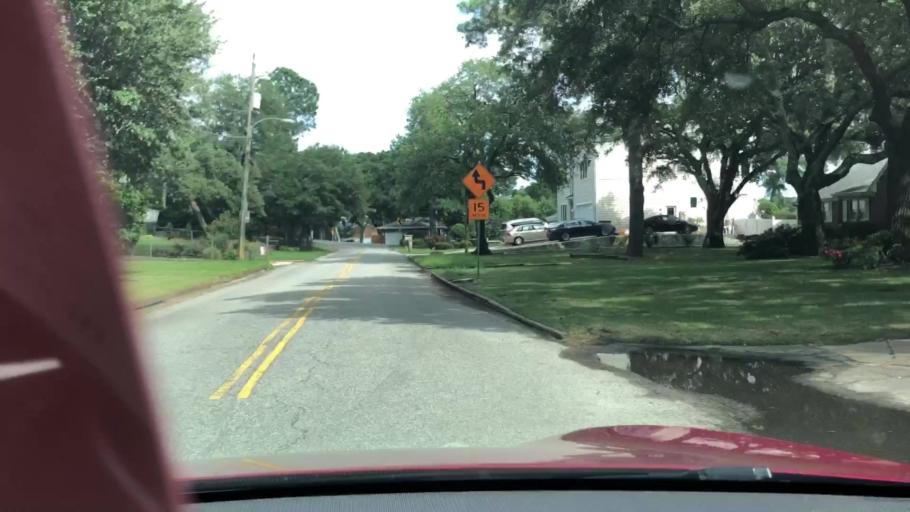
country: US
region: Virginia
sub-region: City of Virginia Beach
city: Virginia Beach
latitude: 36.9065
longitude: -76.0826
